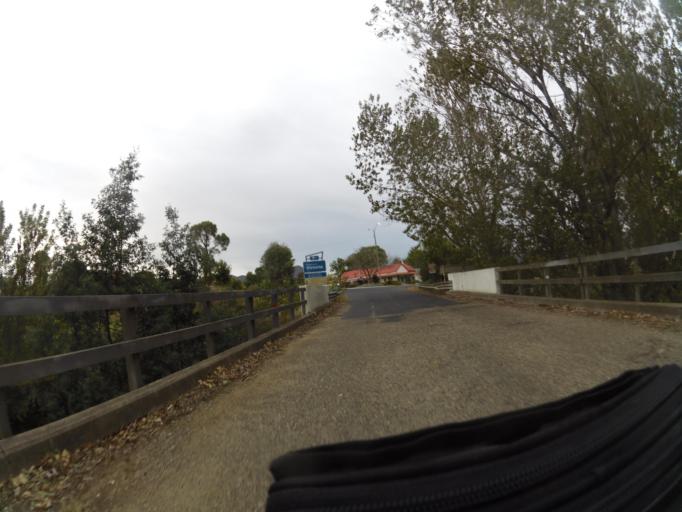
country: AU
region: New South Wales
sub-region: Greater Hume Shire
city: Holbrook
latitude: -36.0461
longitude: 147.9318
